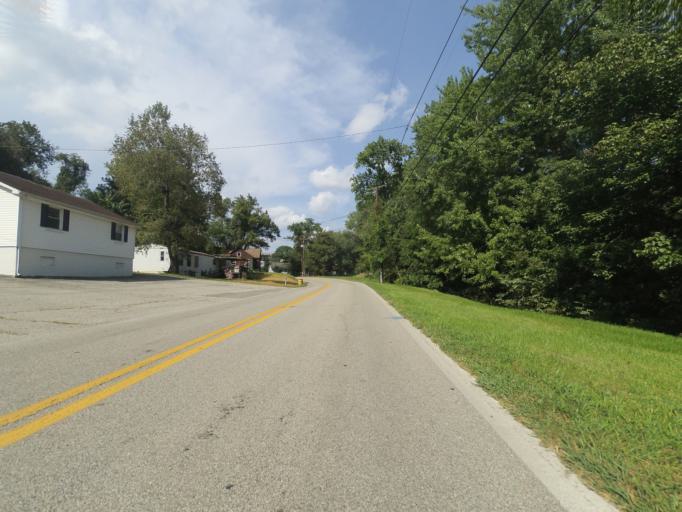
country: US
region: West Virginia
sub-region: Wayne County
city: Ceredo
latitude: 38.3885
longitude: -82.5593
